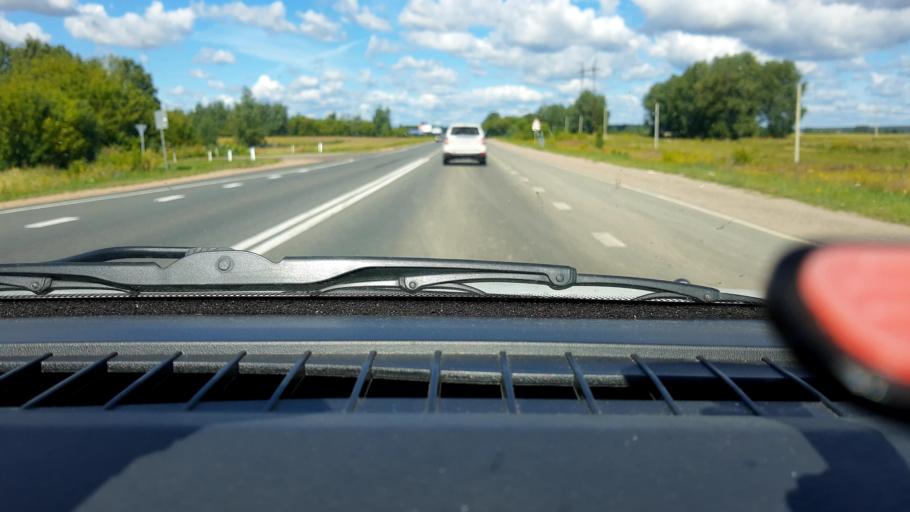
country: RU
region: Nizjnij Novgorod
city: Arzamas
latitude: 55.3106
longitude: 43.9048
